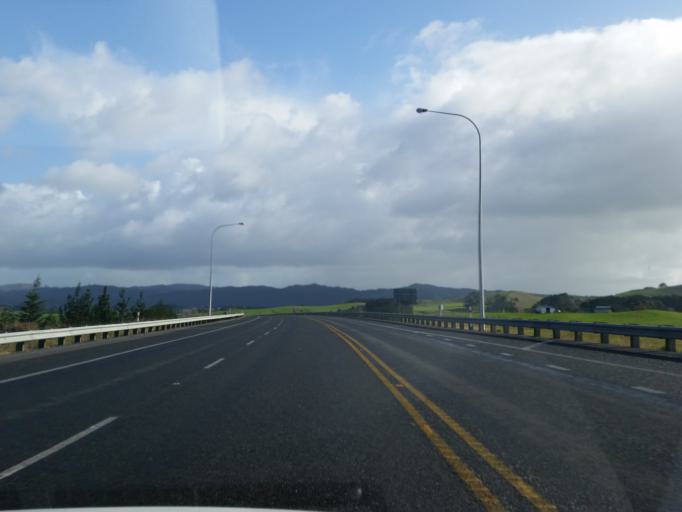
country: NZ
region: Waikato
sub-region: Waikato District
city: Te Kauwhata
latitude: -37.2294
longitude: 175.1607
